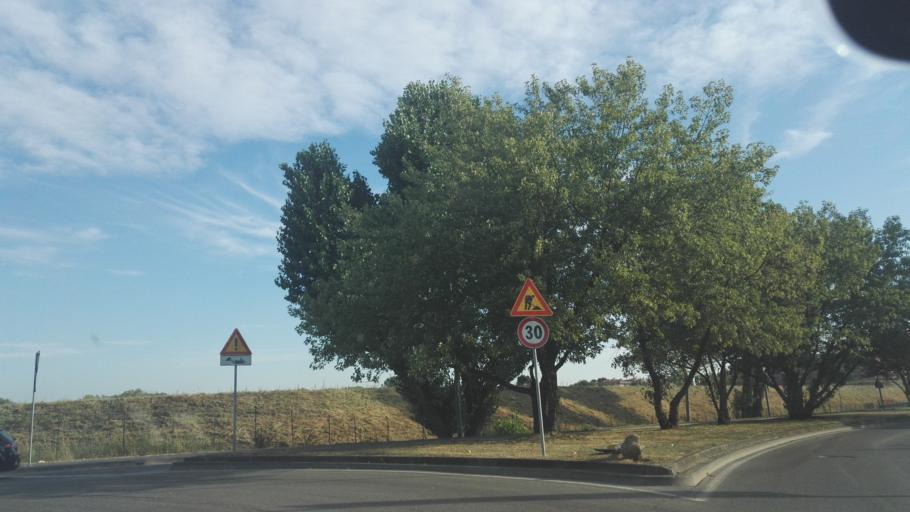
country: IT
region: Lombardy
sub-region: Citta metropolitana di Milano
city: Romano Banco
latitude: 45.4372
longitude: 9.1259
